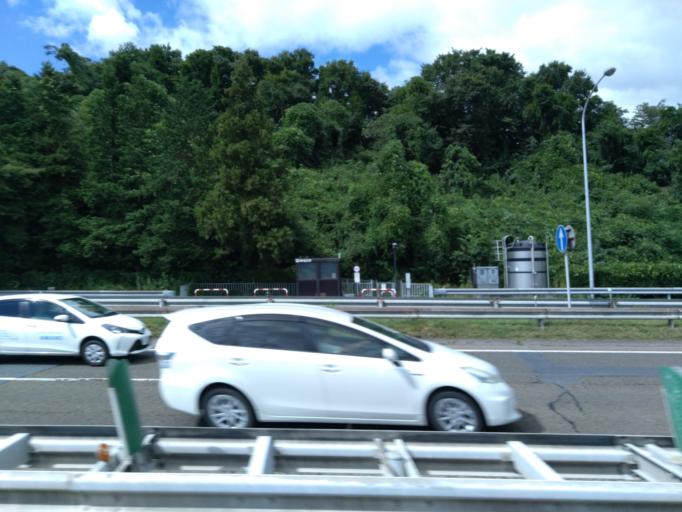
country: JP
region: Miyagi
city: Furukawa
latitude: 38.5185
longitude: 140.9298
